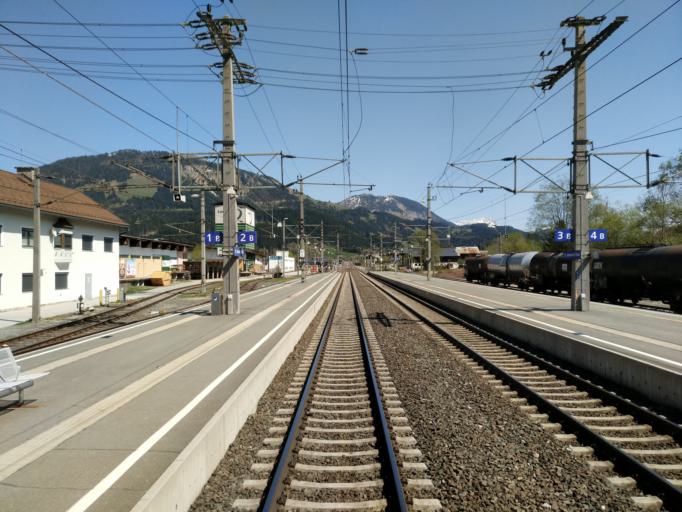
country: AT
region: Tyrol
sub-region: Politischer Bezirk Kitzbuhel
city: Sankt Johann in Tirol
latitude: 47.5196
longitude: 12.4310
